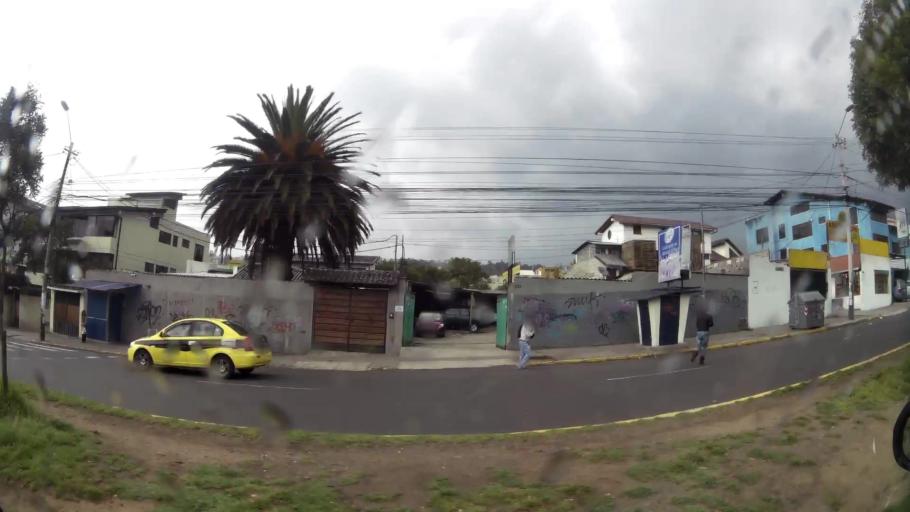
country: EC
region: Pichincha
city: Quito
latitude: -0.1054
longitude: -78.4919
